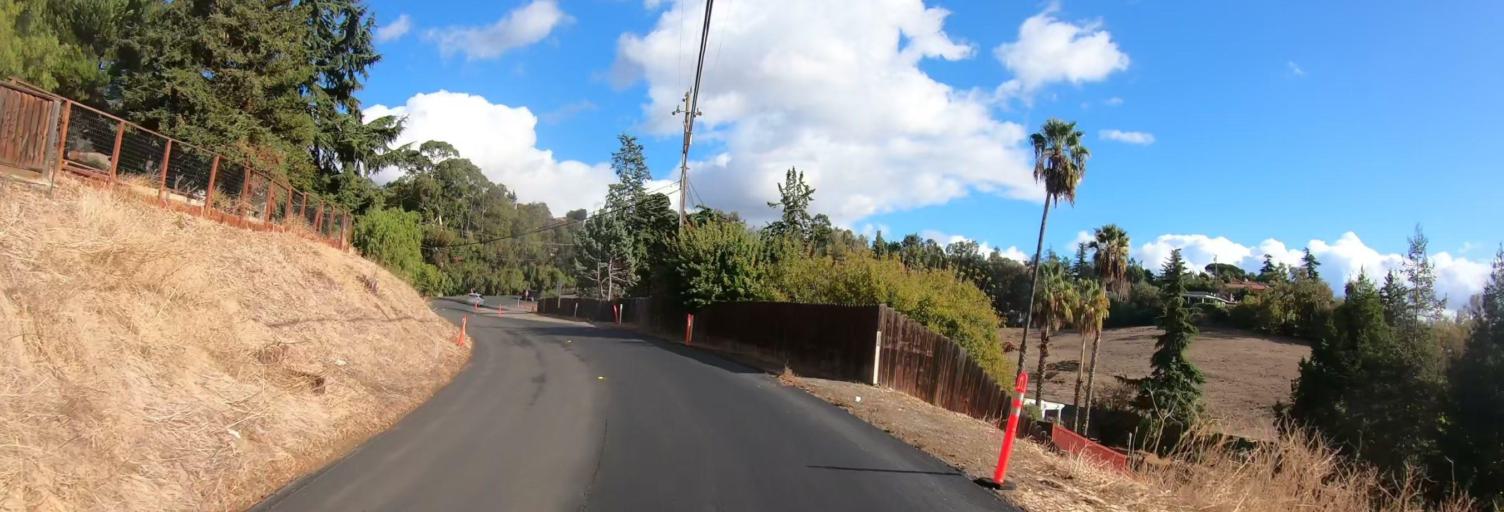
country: US
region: California
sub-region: Santa Clara County
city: East Foothills
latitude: 37.3770
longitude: -121.8035
